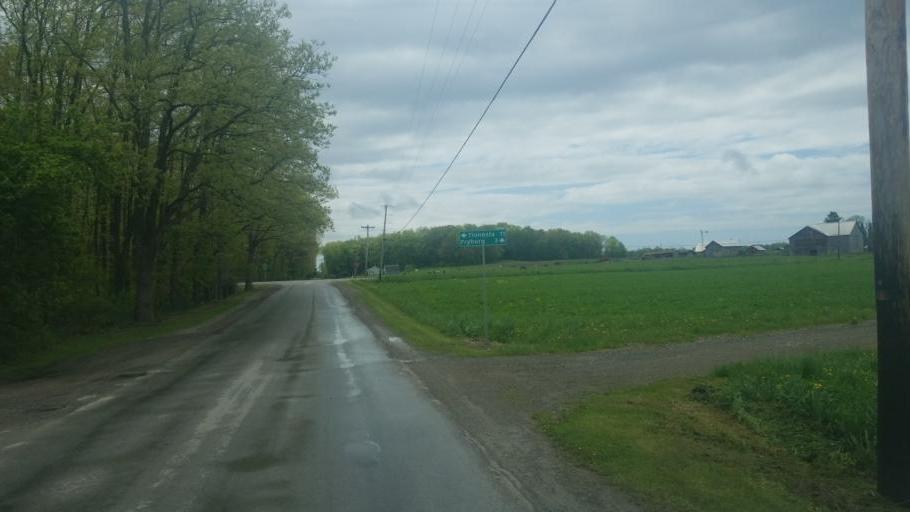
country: US
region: Pennsylvania
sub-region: Forest County
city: Tionesta
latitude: 41.3769
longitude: -79.3887
